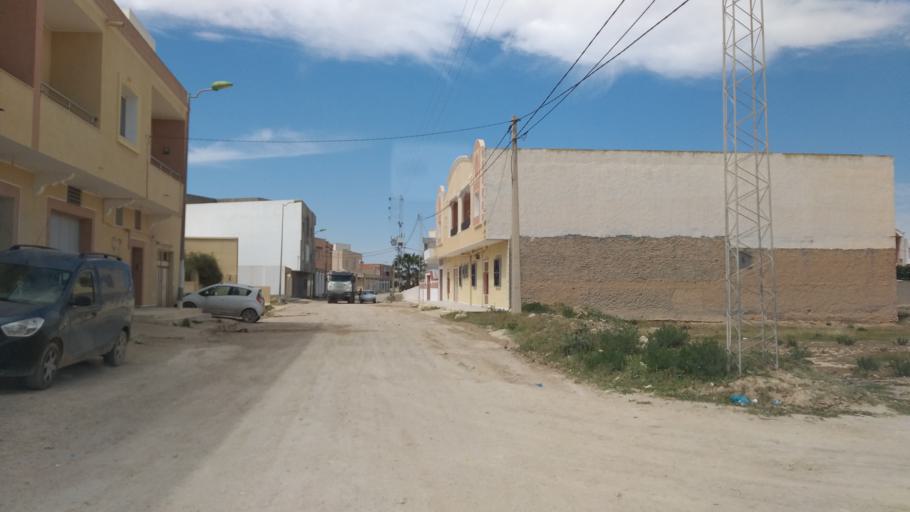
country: TN
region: Al Mahdiyah
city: El Jem
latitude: 35.3032
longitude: 10.6962
